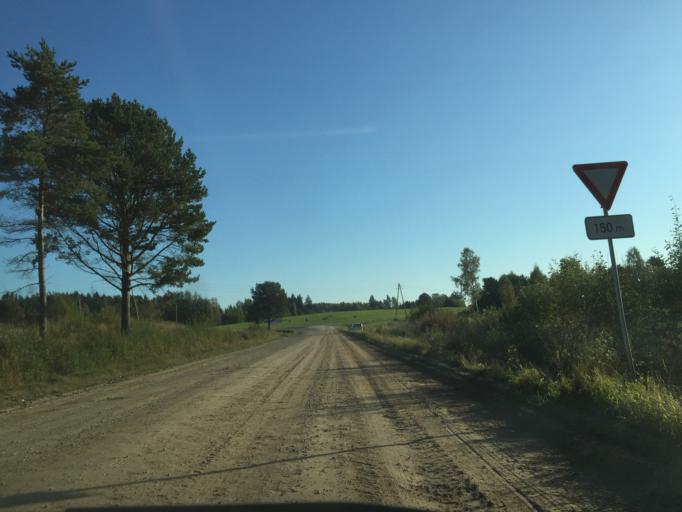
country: LV
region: Vecpiebalga
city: Vecpiebalga
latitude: 57.0770
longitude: 25.7594
